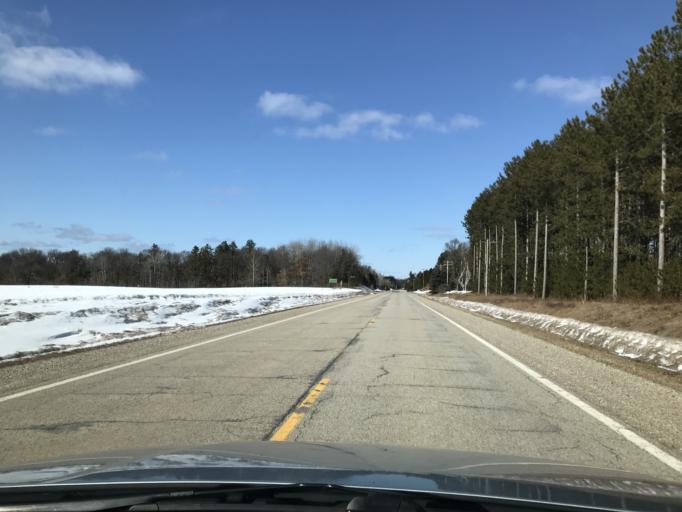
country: US
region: Wisconsin
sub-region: Marinette County
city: Peshtigo
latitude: 45.3239
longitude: -88.1020
